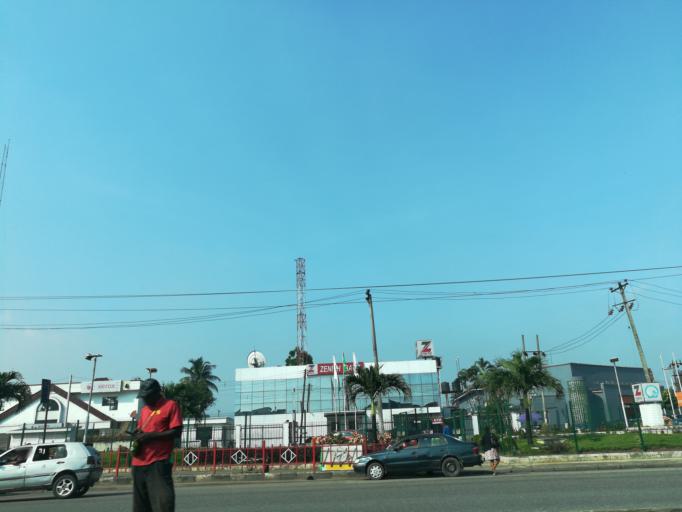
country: NG
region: Rivers
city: Port Harcourt
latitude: 4.8240
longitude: 7.0062
